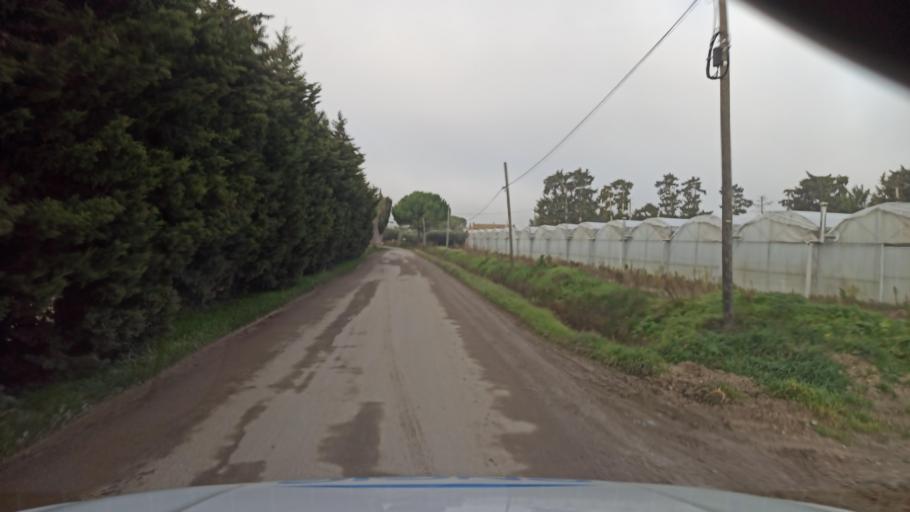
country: FR
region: Provence-Alpes-Cote d'Azur
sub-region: Departement des Bouches-du-Rhone
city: Rognonas
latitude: 43.8870
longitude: 4.8153
